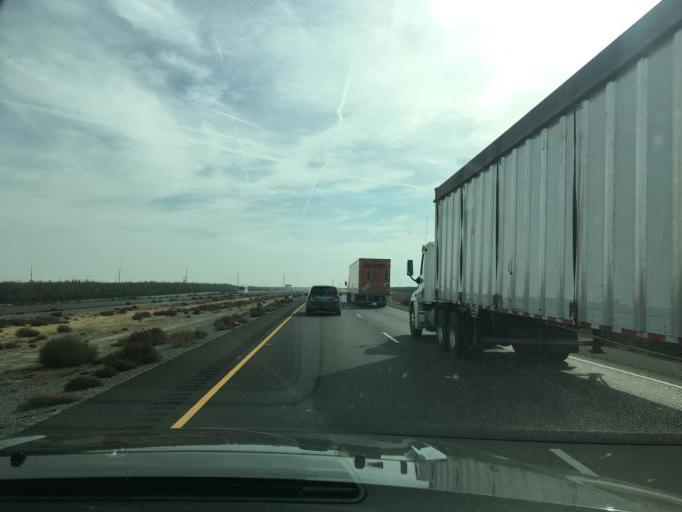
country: US
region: California
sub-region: Kings County
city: Kettleman City
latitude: 35.9526
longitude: -119.9308
